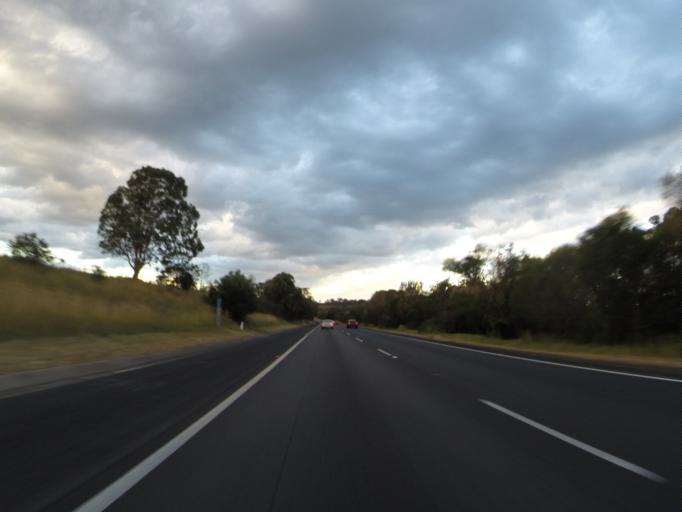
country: AU
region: New South Wales
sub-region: Campbelltown Municipality
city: Glen Alpine
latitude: -34.1233
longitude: 150.7535
